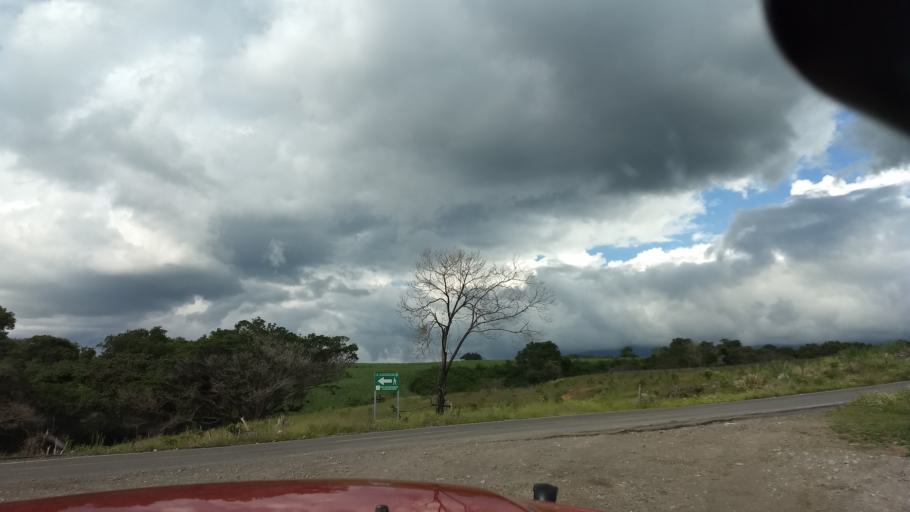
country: MX
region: Colima
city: Suchitlan
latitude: 19.4683
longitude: -103.7540
